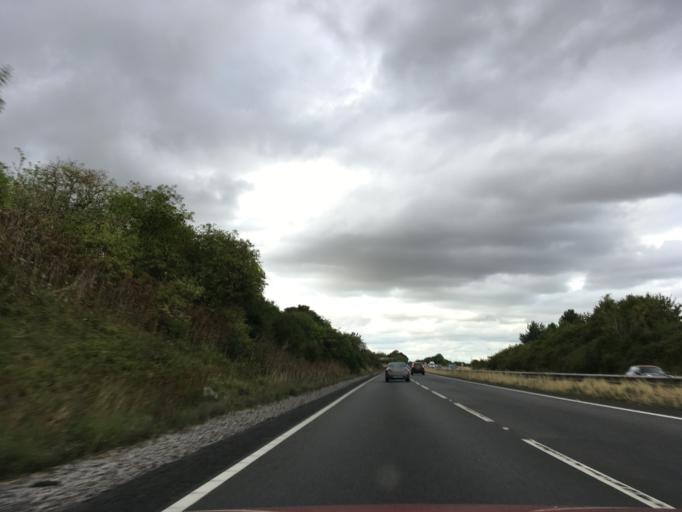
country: GB
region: England
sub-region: Hampshire
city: Kings Worthy
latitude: 51.1559
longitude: -1.3457
